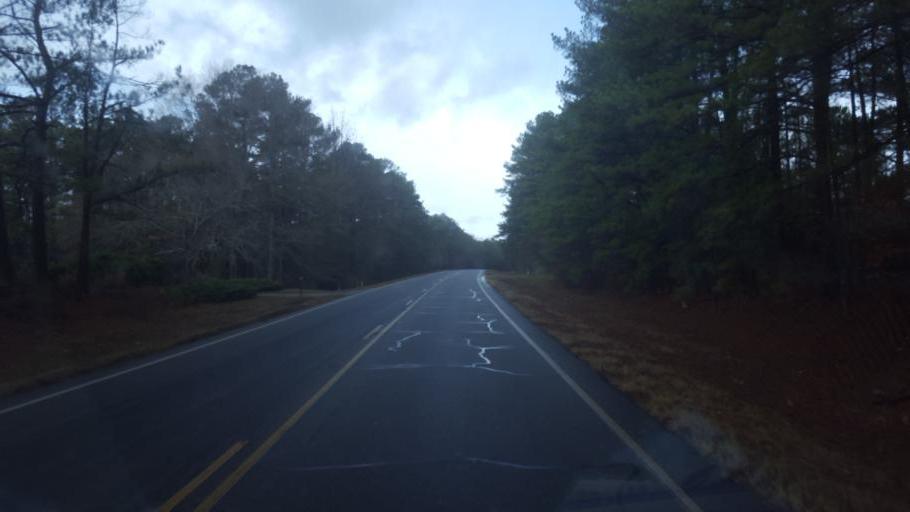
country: US
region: Georgia
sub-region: Butts County
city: Indian Springs
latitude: 33.2270
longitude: -83.8737
